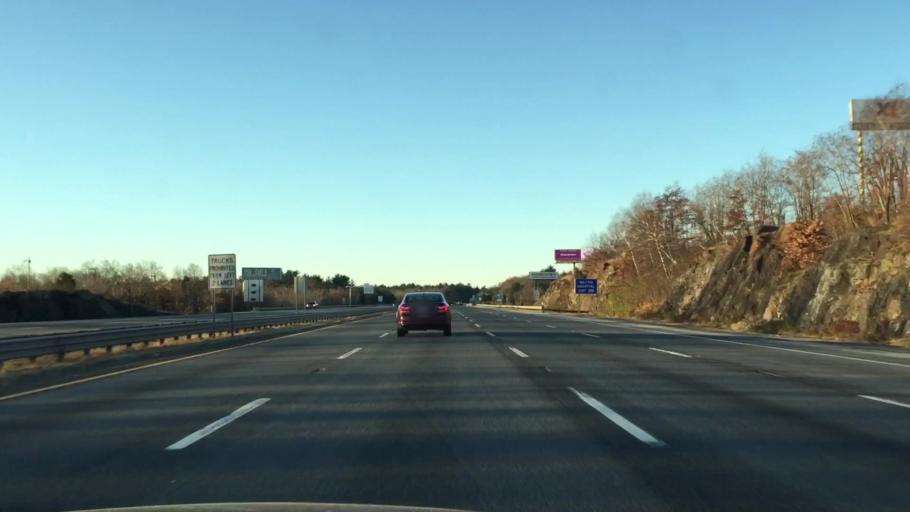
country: US
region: Massachusetts
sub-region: Norfolk County
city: Braintree
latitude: 42.2157
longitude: -71.0337
